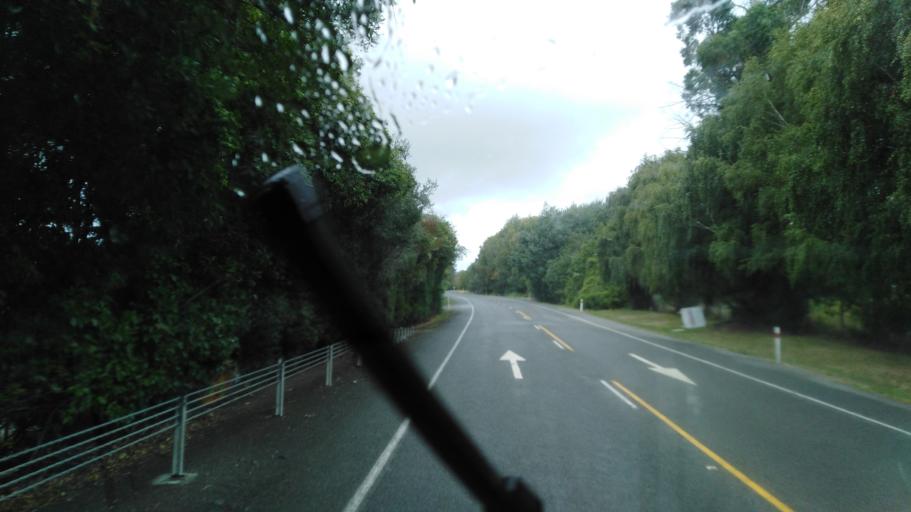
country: NZ
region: Marlborough
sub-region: Marlborough District
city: Blenheim
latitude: -41.4576
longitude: 173.9536
